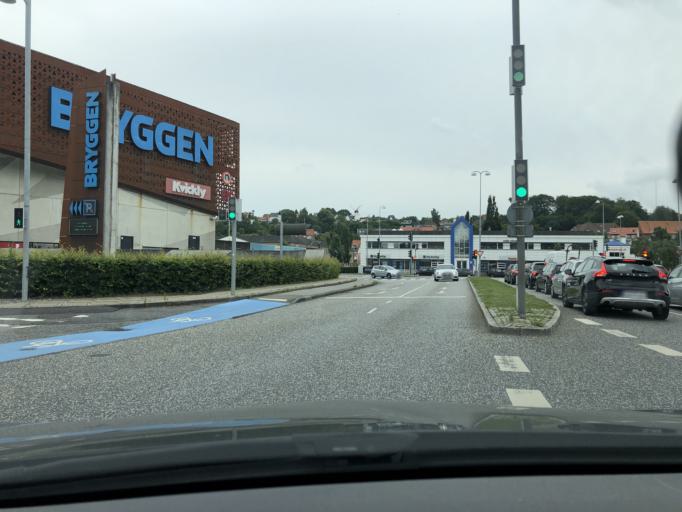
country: DK
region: South Denmark
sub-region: Vejle Kommune
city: Vejle
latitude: 55.7055
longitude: 9.5288
